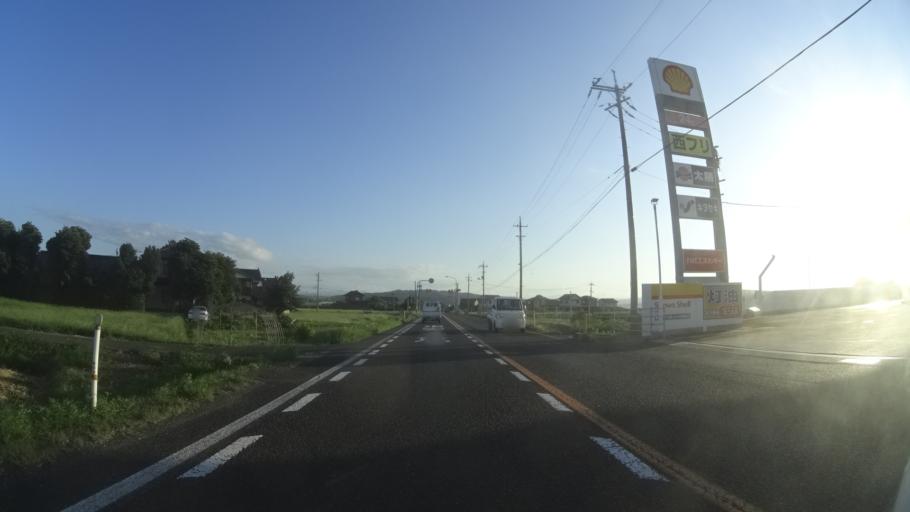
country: JP
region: Tottori
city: Yonago
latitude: 35.4715
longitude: 133.4340
